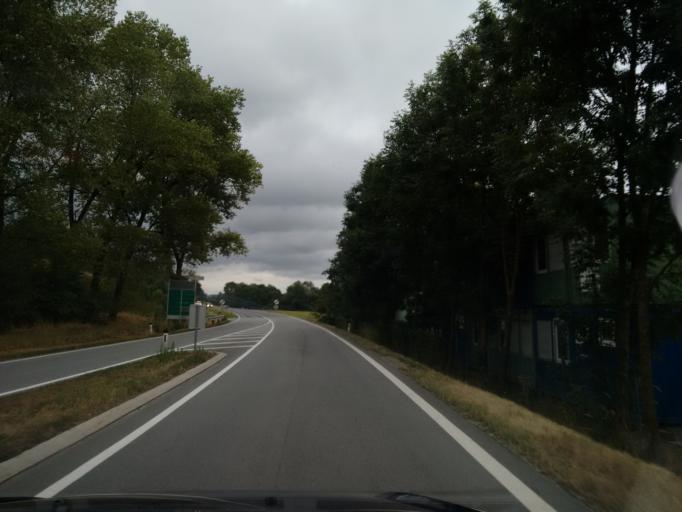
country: AT
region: Upper Austria
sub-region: Politischer Bezirk Grieskirchen
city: Bad Schallerbach
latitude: 48.2208
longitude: 13.9472
